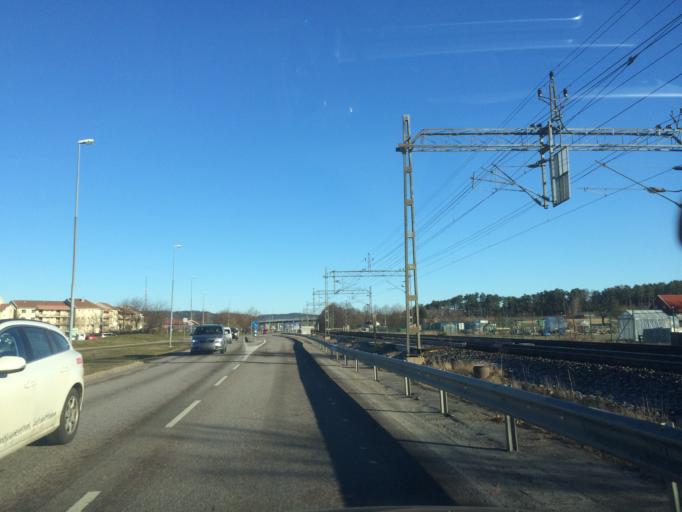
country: SE
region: Halland
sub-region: Kungsbacka Kommun
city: Kungsbacka
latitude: 57.4959
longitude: 12.0800
